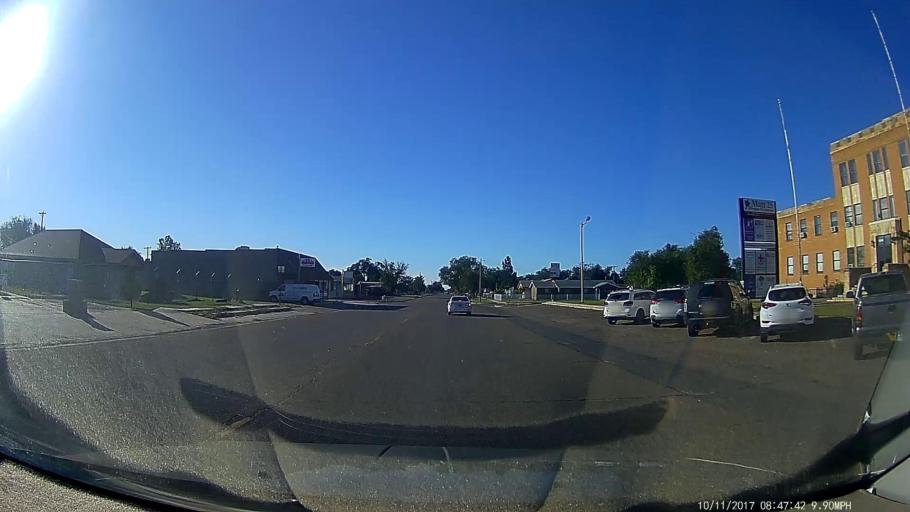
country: US
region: New Mexico
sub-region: Curry County
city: Clovis
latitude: 34.4104
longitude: -103.2140
